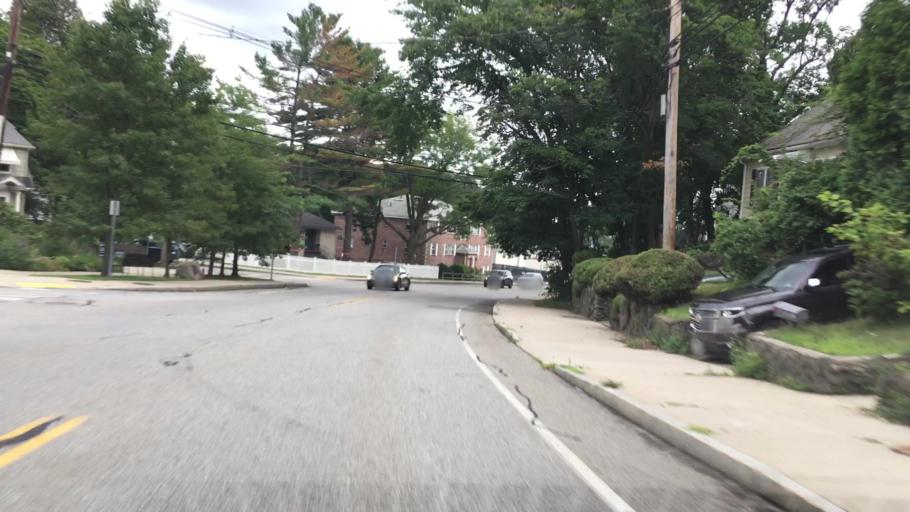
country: US
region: Massachusetts
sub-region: Middlesex County
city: Arlington
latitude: 42.4286
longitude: -71.1749
